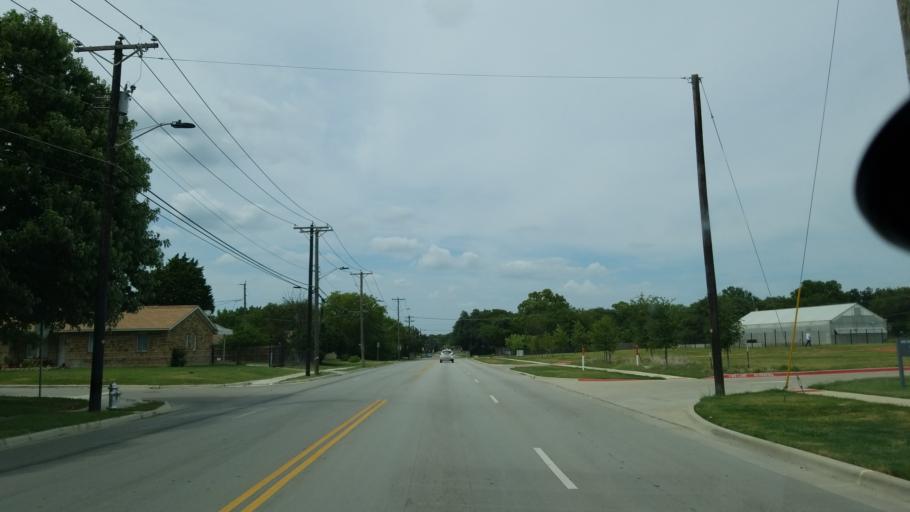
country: US
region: Texas
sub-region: Tarrant County
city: Arlington
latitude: 32.7102
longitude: -97.0854
